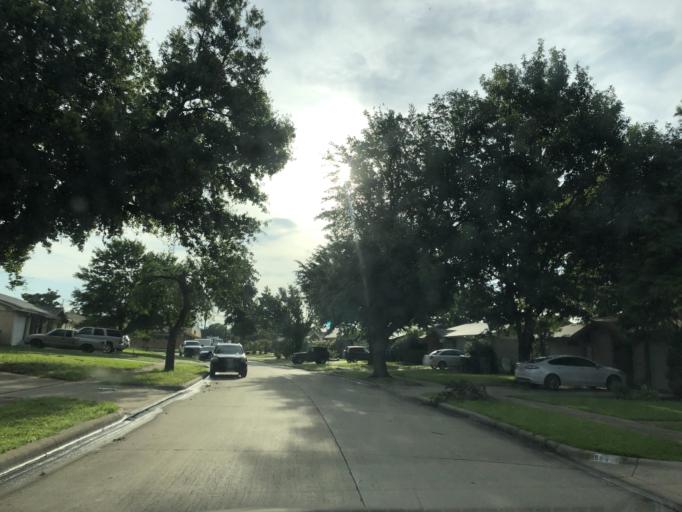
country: US
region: Texas
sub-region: Dallas County
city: Sunnyvale
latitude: 32.8471
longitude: -96.5984
